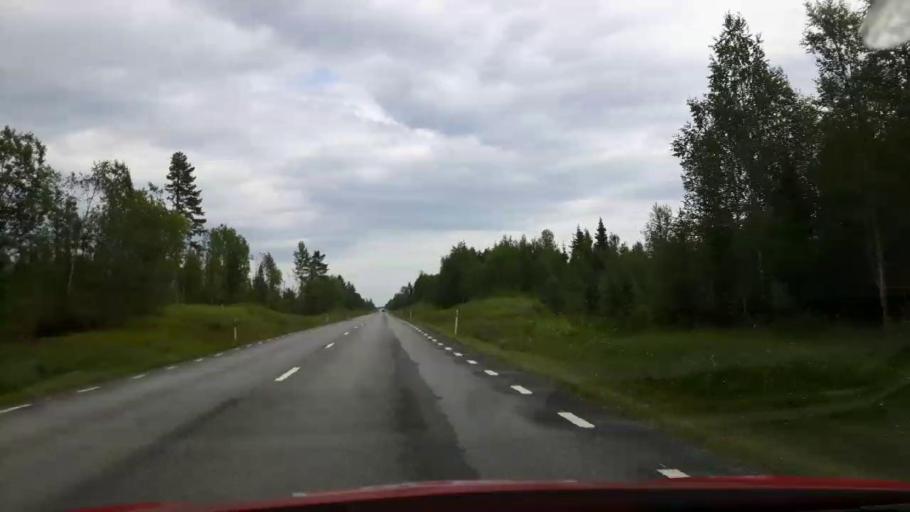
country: SE
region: Jaemtland
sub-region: Stroemsunds Kommun
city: Stroemsund
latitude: 63.6863
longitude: 15.4115
